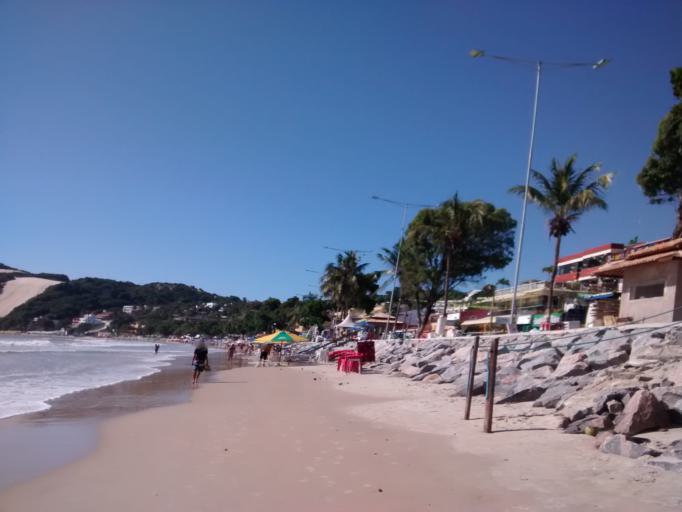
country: BR
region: Rio Grande do Norte
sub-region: Natal
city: Natal
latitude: -5.8814
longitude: -35.1711
